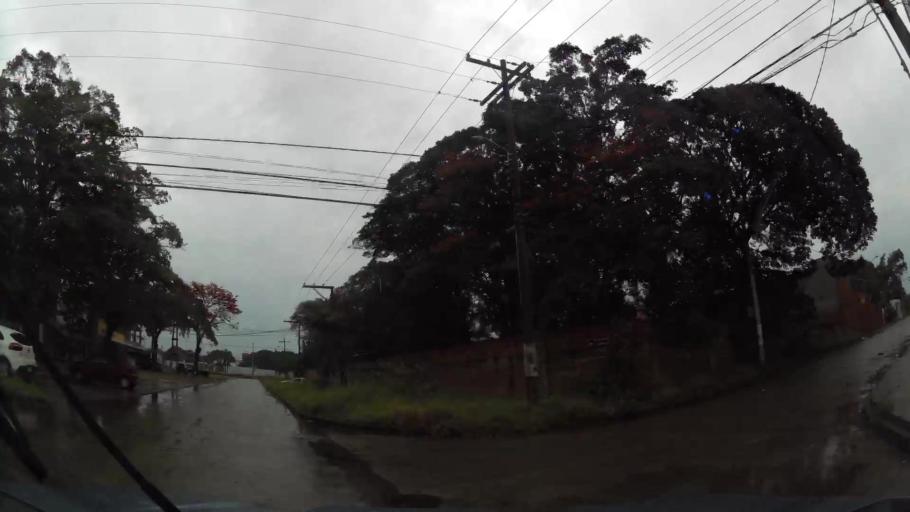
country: BO
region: Santa Cruz
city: Santa Cruz de la Sierra
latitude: -17.7869
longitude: -63.2156
